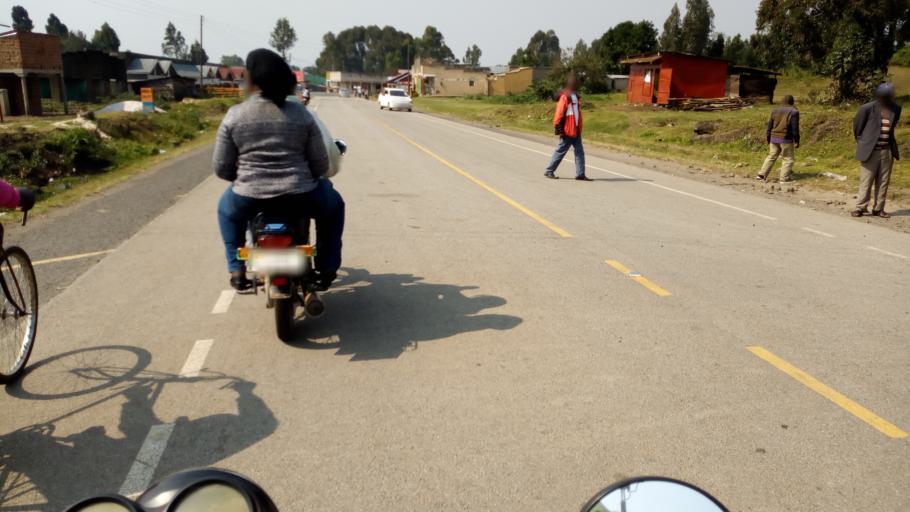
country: UG
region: Western Region
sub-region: Kisoro District
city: Kisoro
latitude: -1.3375
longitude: 29.7382
